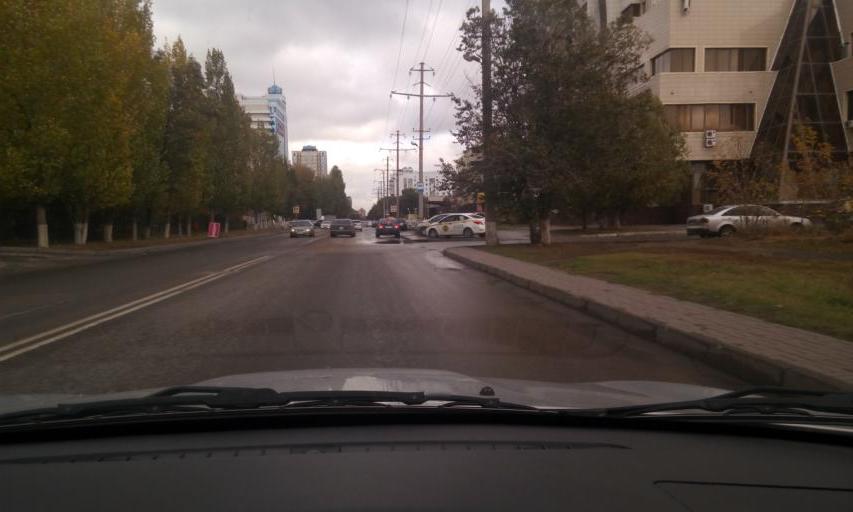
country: KZ
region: Astana Qalasy
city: Astana
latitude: 51.1654
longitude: 71.4033
